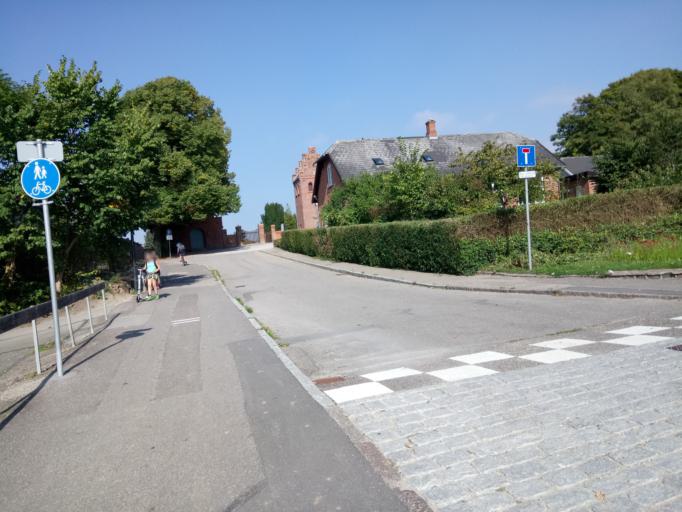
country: DK
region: Capital Region
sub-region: Egedal Kommune
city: Olstykke
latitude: 55.7820
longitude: 12.1741
